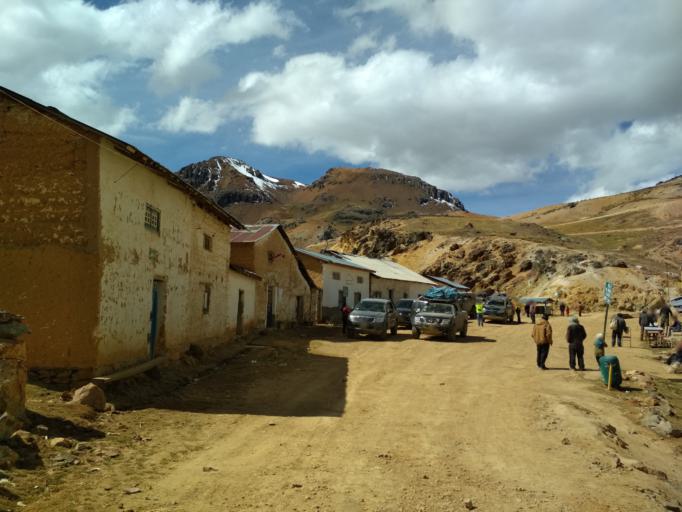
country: PE
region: Huancavelica
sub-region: Provincia de Huancavelica
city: Acobambilla
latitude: -12.6369
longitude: -75.5323
